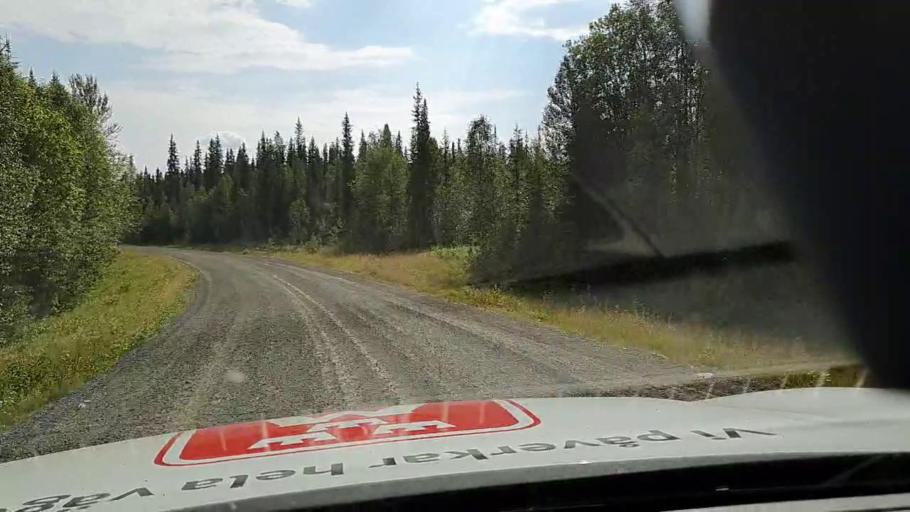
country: SE
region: Vaesterbotten
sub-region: Storumans Kommun
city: Fristad
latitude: 65.5405
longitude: 16.7994
